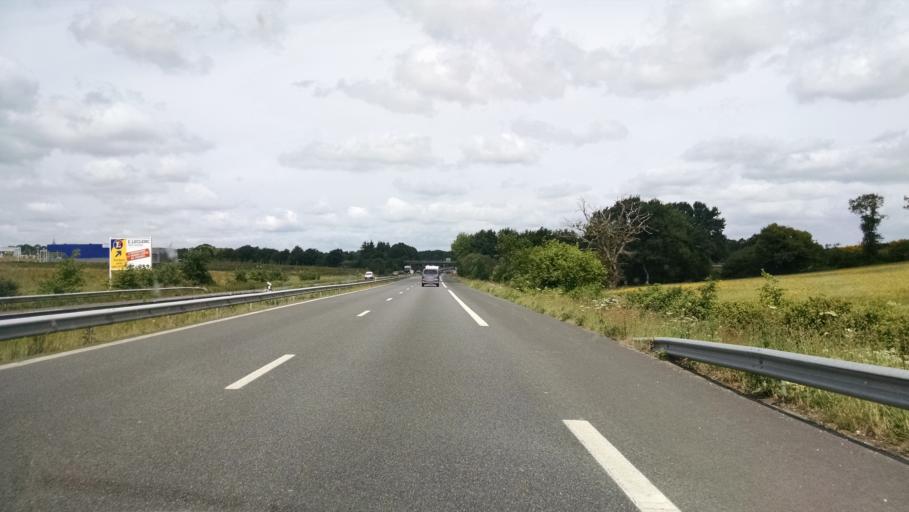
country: FR
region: Pays de la Loire
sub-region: Departement de la Loire-Atlantique
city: Pontchateau
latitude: 47.4350
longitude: -2.0696
